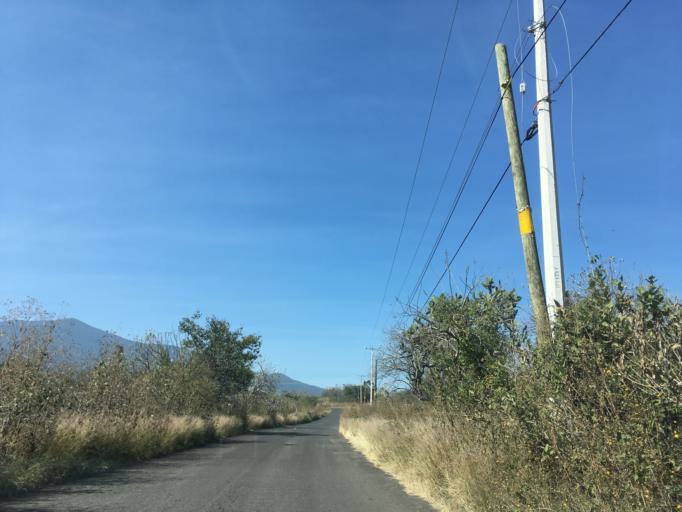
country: MX
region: Michoacan
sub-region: Morelia
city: La Mintzita (Piedra Dura)
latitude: 19.6491
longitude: -101.2979
